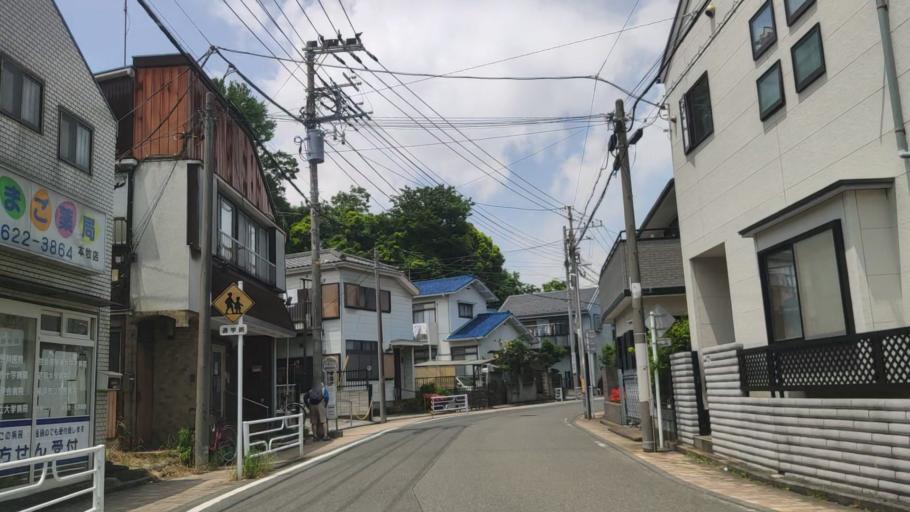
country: JP
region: Kanagawa
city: Yokohama
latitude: 35.4292
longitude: 139.6581
